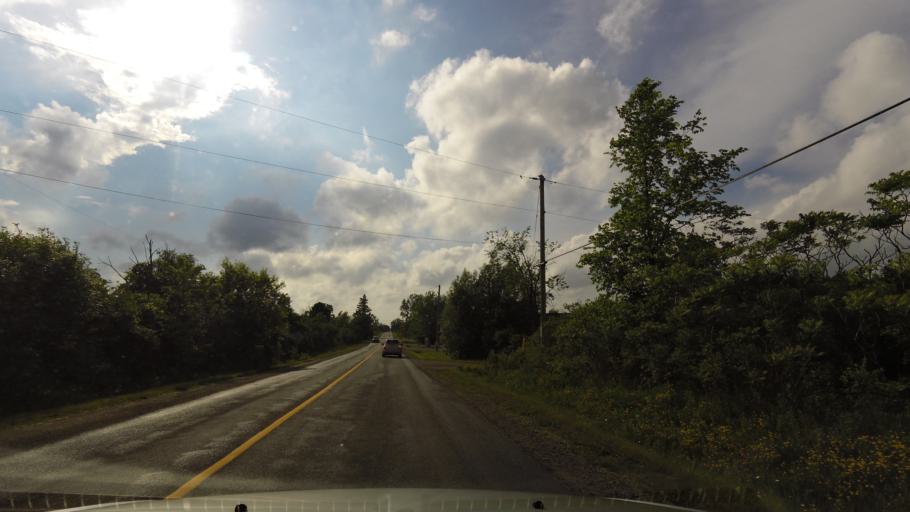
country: CA
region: Ontario
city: Ancaster
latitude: 43.0063
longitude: -80.0606
